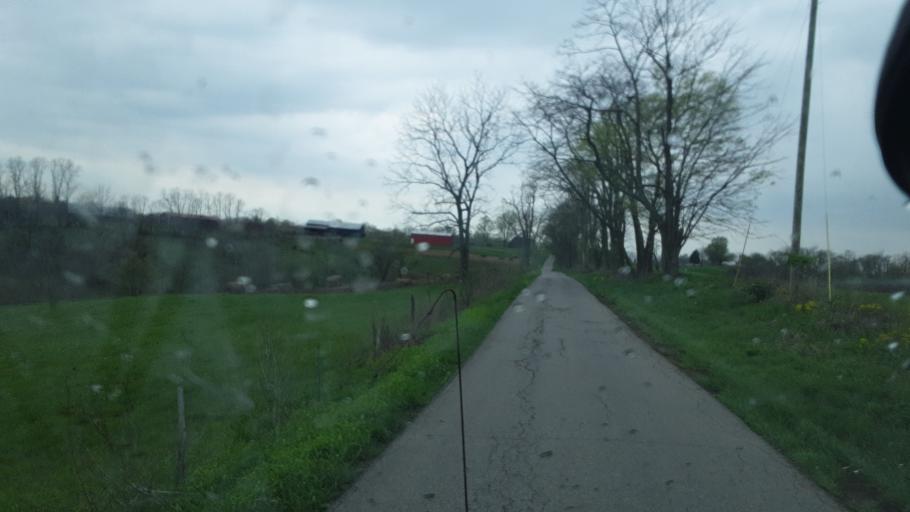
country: US
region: Kentucky
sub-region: Owen County
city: Owenton
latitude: 38.6745
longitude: -84.8071
